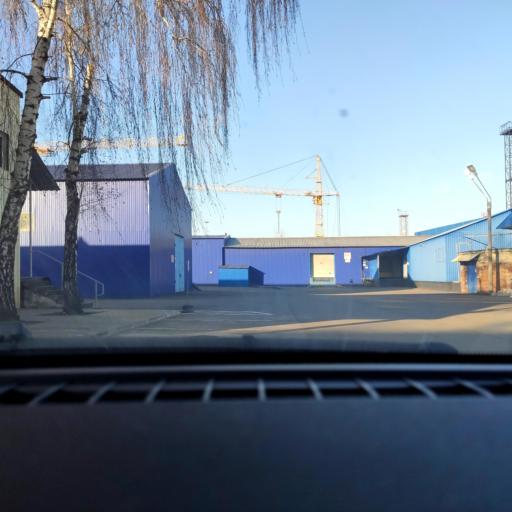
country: RU
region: Voronezj
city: Voronezh
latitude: 51.6501
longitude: 39.2680
